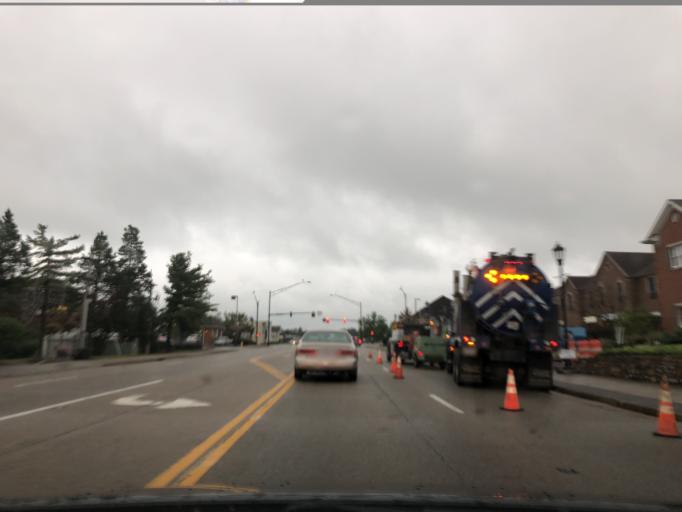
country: US
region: Ohio
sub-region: Hamilton County
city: Blue Ash
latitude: 39.2300
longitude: -84.3772
